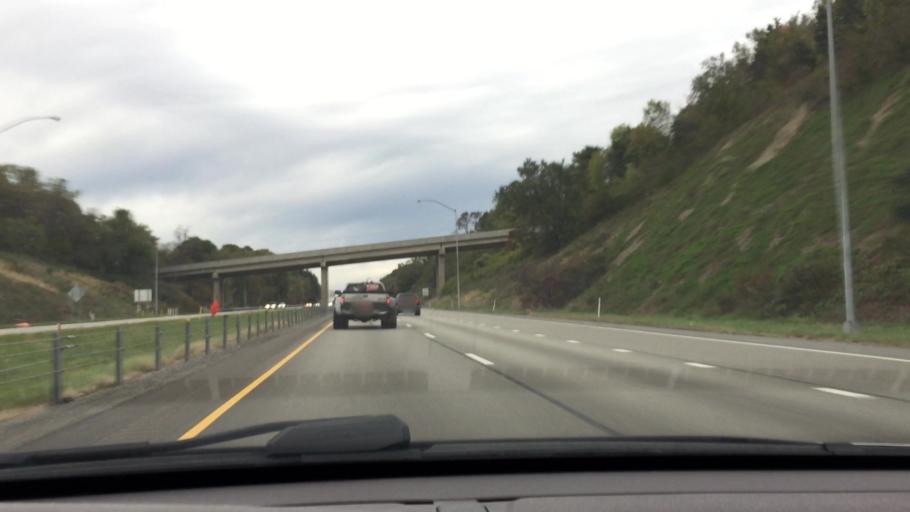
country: US
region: Pennsylvania
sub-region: Beaver County
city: Ambridge
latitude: 40.5604
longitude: -80.2796
